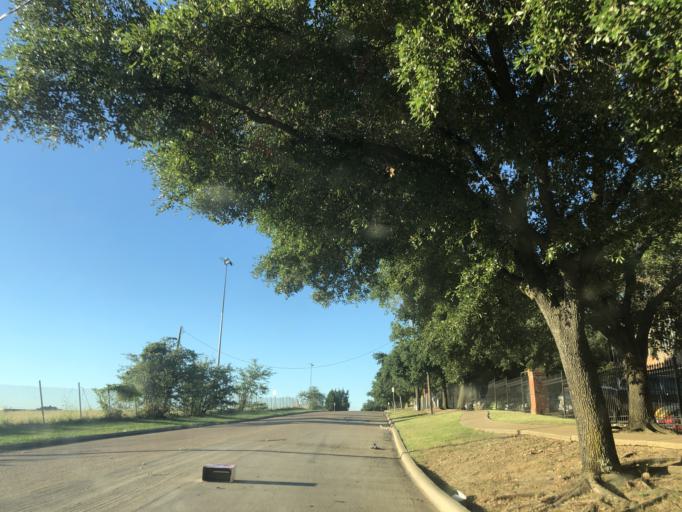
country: US
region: Texas
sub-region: Dallas County
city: Garland
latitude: 32.8398
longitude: -96.6343
